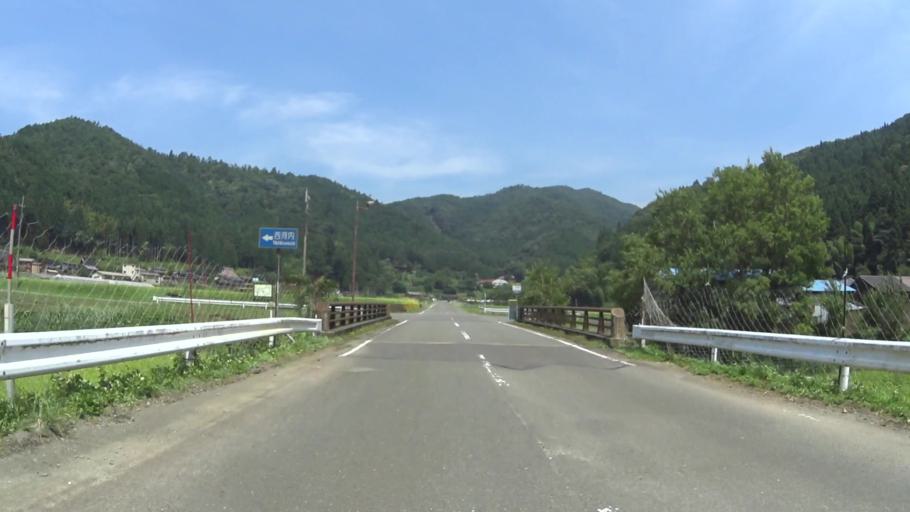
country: JP
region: Kyoto
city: Ayabe
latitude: 35.2983
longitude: 135.4256
